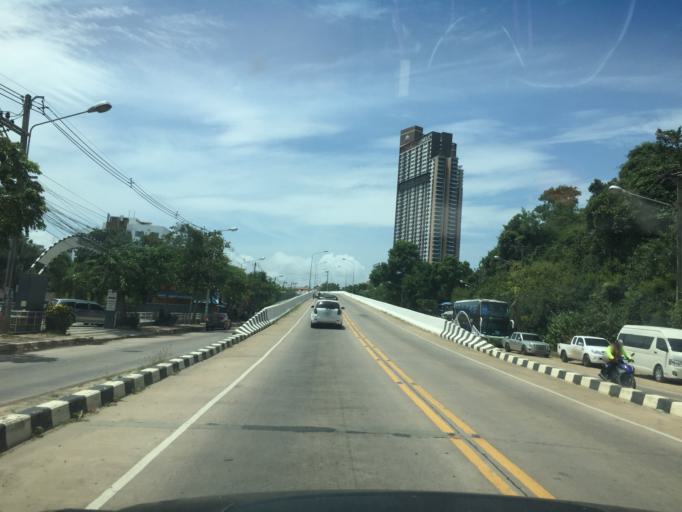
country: TH
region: Chon Buri
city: Phatthaya
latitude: 12.9227
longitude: 100.8680
